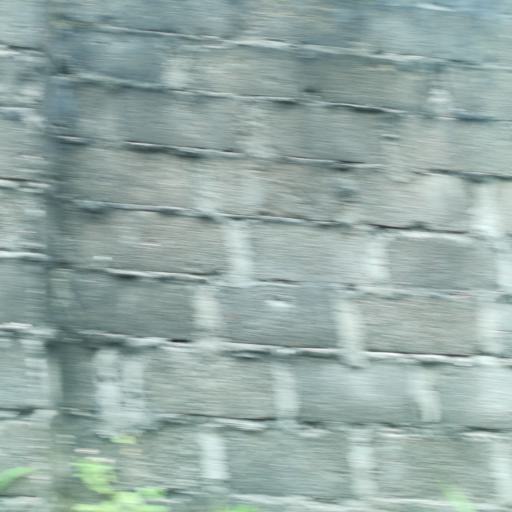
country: NG
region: Rivers
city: Port Harcourt
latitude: 4.7798
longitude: 7.0427
